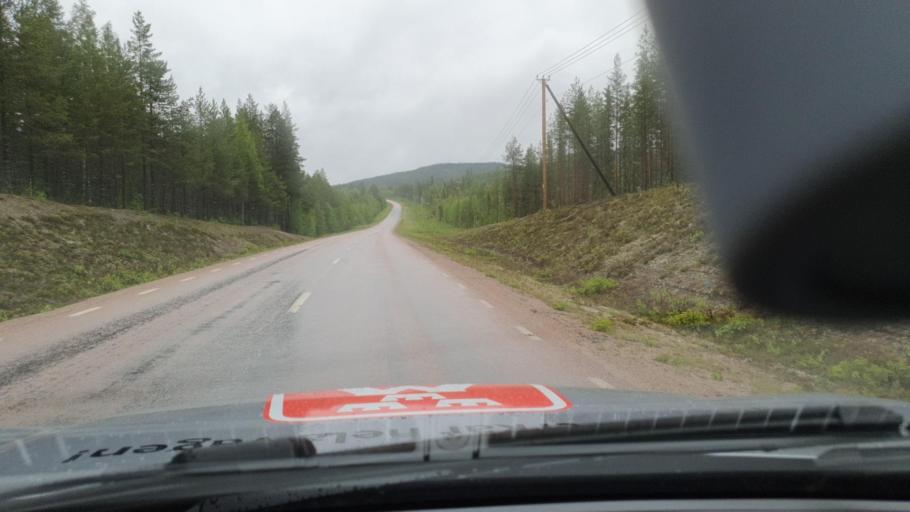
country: SE
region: Norrbotten
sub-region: Overkalix Kommun
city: OEverkalix
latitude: 66.4091
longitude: 22.9569
